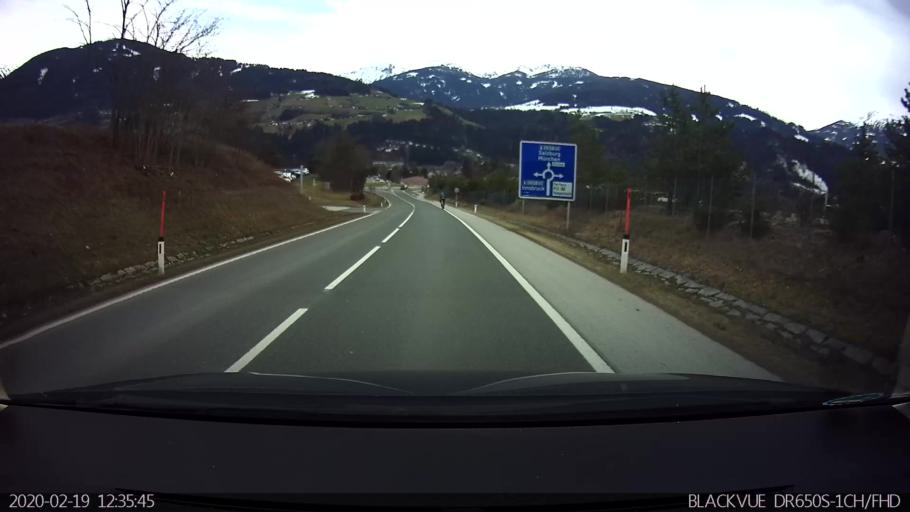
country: AT
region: Tyrol
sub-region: Politischer Bezirk Schwaz
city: Vomp
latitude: 47.3314
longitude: 11.6734
